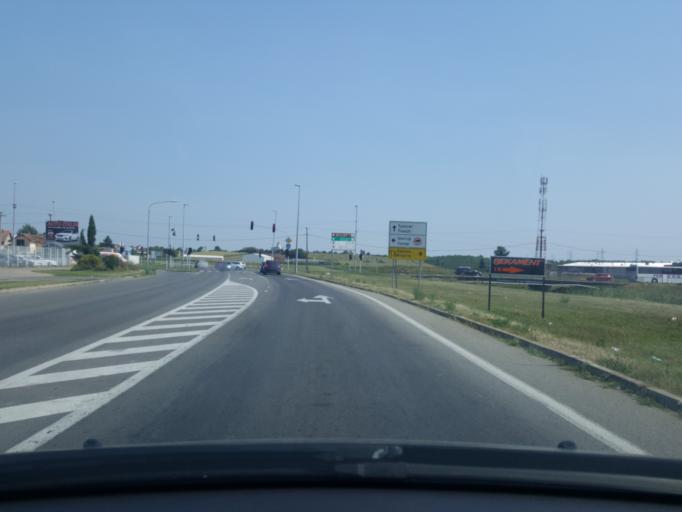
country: RS
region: Central Serbia
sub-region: Macvanski Okrug
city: Sabac
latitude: 44.7410
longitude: 19.6745
